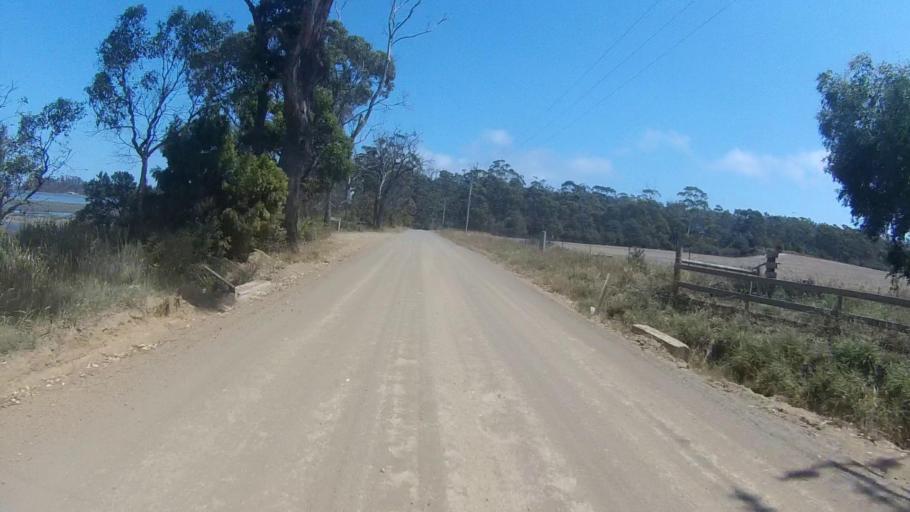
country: AU
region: Tasmania
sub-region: Sorell
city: Sorell
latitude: -42.8445
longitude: 147.8463
